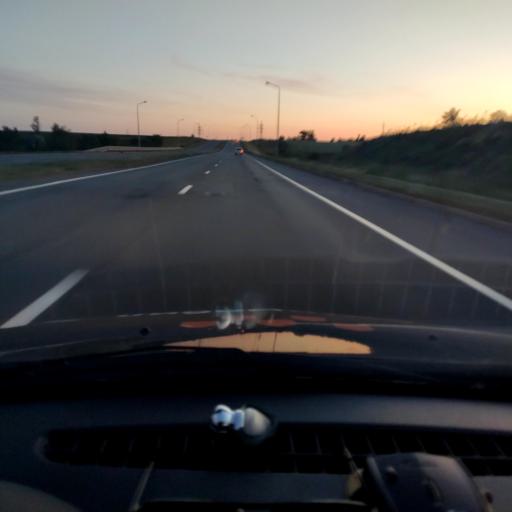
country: RU
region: Belgorod
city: Staryy Oskol
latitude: 51.3244
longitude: 37.7215
